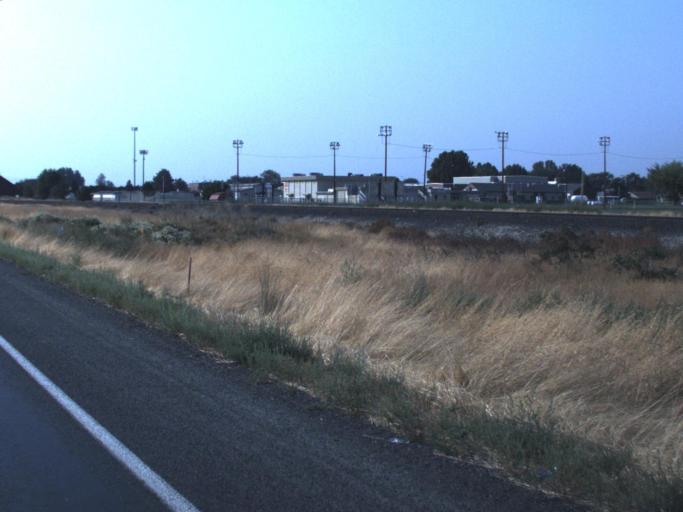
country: US
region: Washington
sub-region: Yakima County
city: Mabton
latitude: 46.2098
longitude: -119.9920
